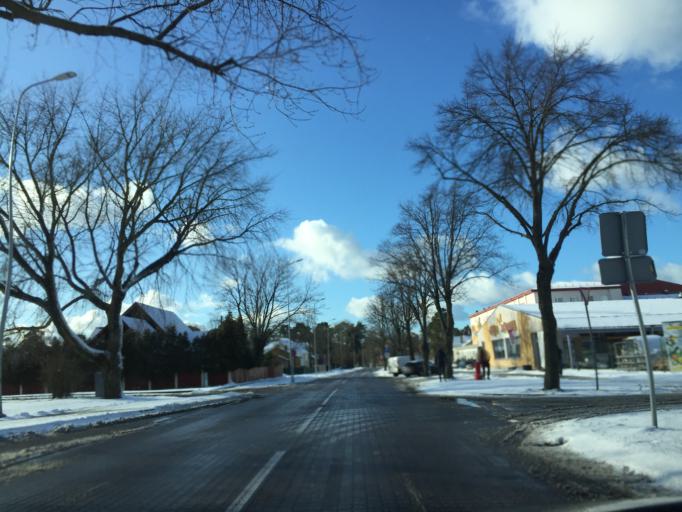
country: LV
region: Ventspils
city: Ventspils
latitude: 57.3858
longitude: 21.5459
